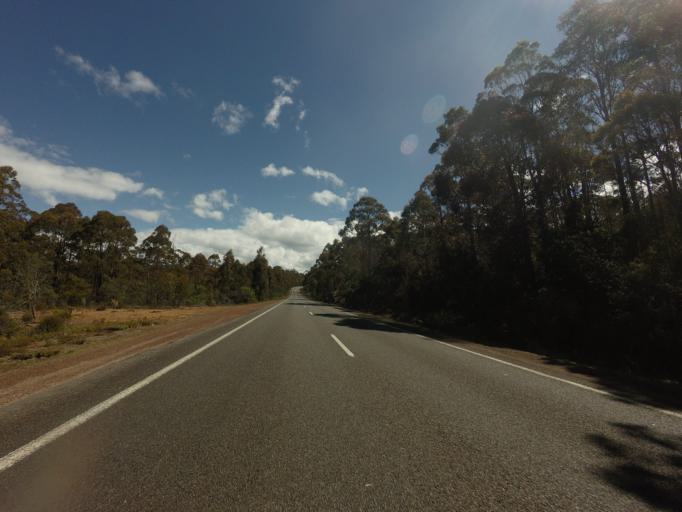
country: AU
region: Tasmania
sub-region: Northern Midlands
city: Evandale
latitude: -42.0148
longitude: 147.8608
